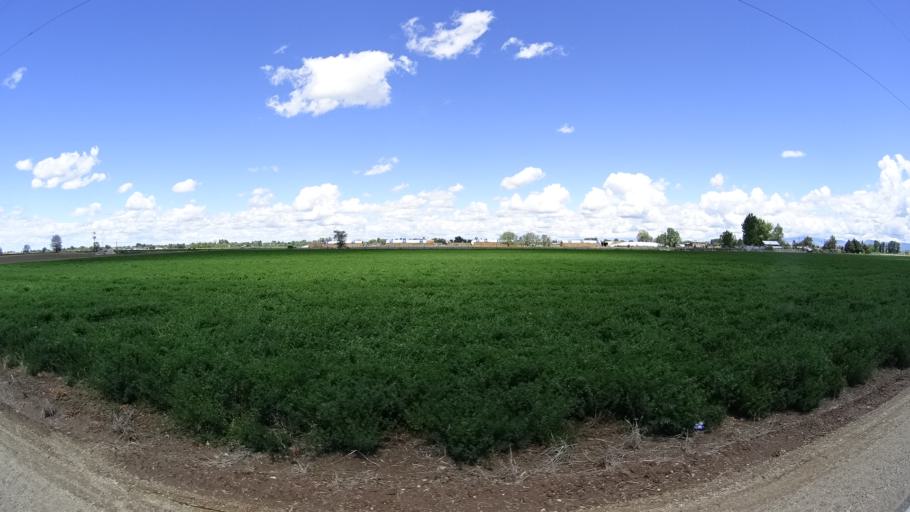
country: US
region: Idaho
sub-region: Ada County
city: Kuna
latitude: 43.5463
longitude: -116.4572
